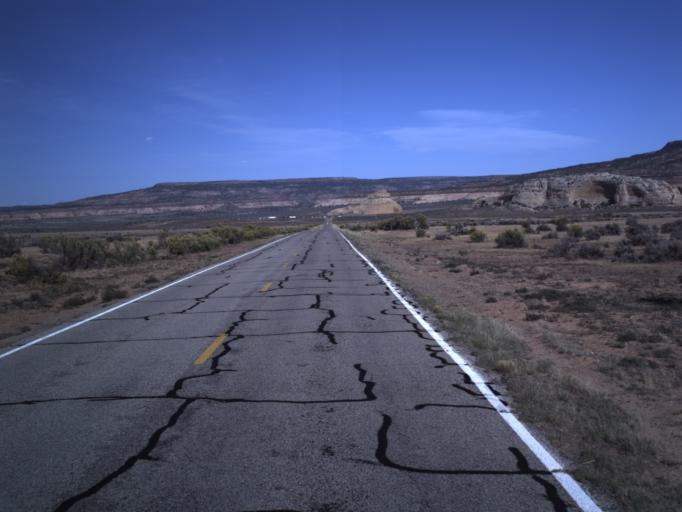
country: US
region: Utah
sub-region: San Juan County
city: Monticello
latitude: 38.0672
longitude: -109.3762
